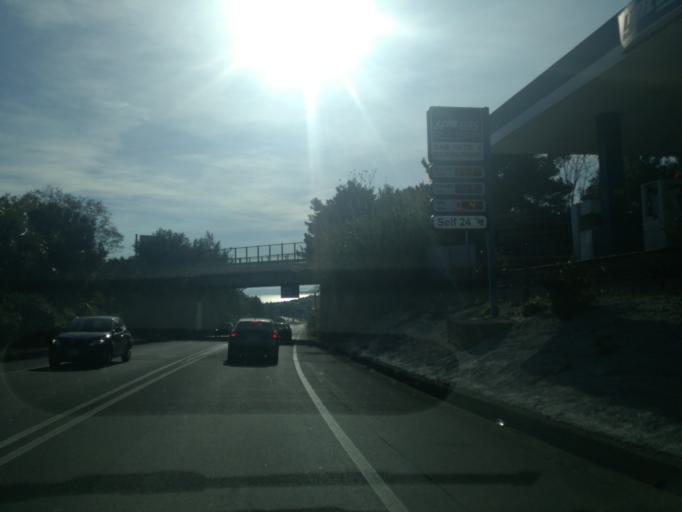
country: IT
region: Sicily
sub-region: Catania
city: Vambolieri
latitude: 37.5830
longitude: 15.1694
